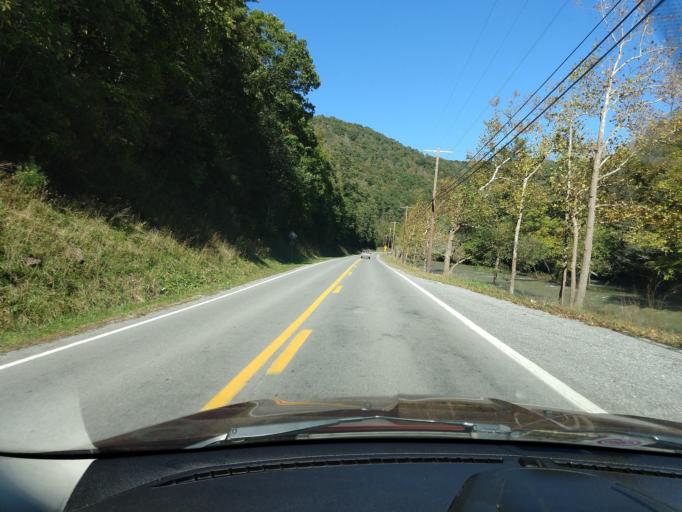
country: US
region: West Virginia
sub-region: Pocahontas County
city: Marlinton
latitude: 38.2114
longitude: -80.0488
